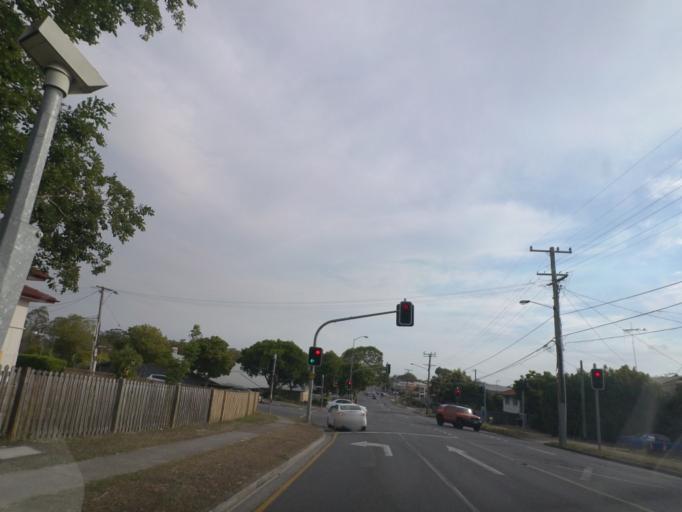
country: AU
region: Queensland
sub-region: Brisbane
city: Coopers Plains
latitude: -27.5570
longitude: 153.0407
